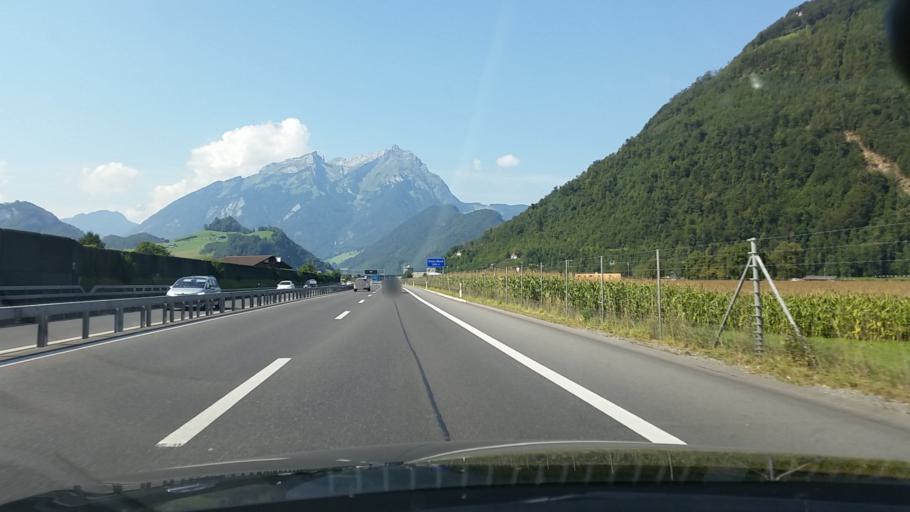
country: CH
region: Nidwalden
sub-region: Nidwalden
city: Stans
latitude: 46.9657
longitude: 8.3749
